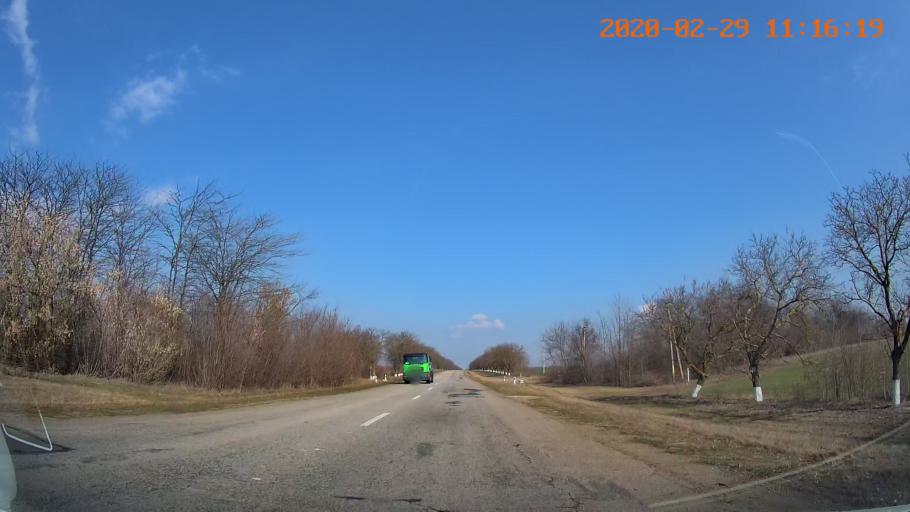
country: MD
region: Telenesti
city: Dubasari
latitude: 47.3071
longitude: 29.1675
